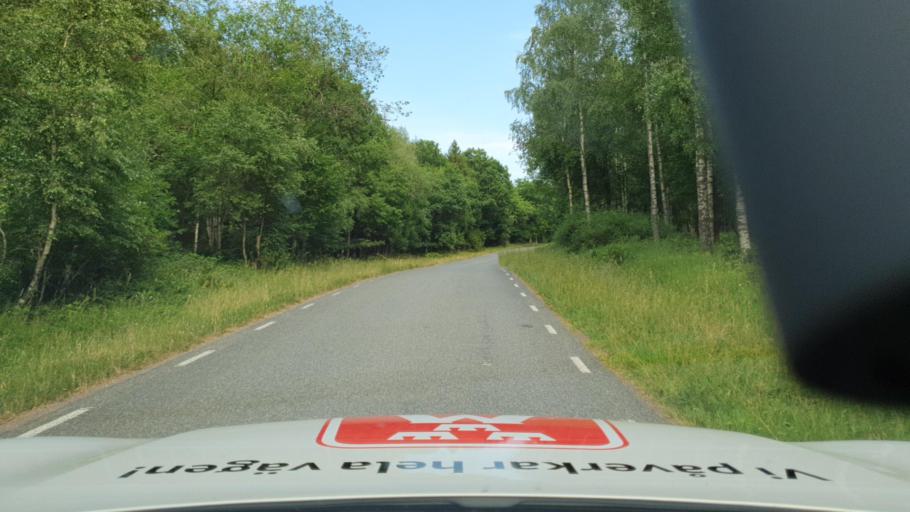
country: SE
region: Skane
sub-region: Kristianstads Kommun
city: Degeberga
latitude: 55.6918
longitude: 14.0803
